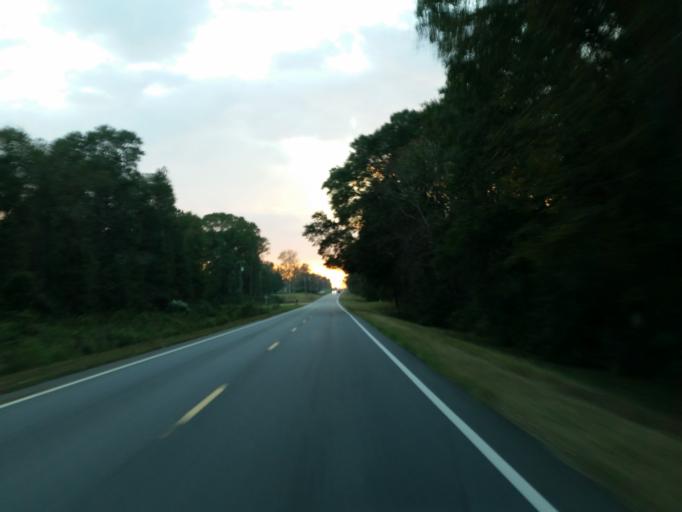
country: US
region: Georgia
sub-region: Pulaski County
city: Hawkinsville
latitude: 32.2081
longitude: -83.5479
